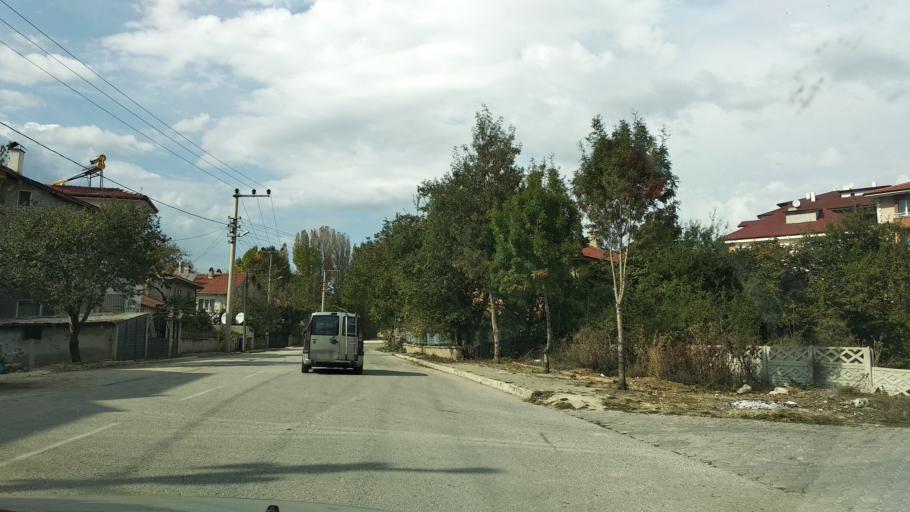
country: TR
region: Bolu
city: Bolu
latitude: 40.7292
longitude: 31.5867
